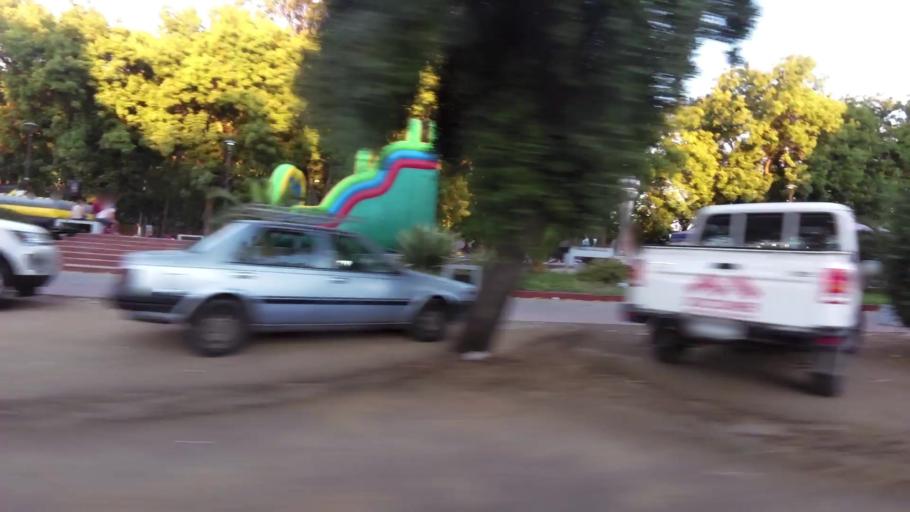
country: CL
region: Maule
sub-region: Provincia de Curico
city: Curico
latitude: -34.9838
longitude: -71.2345
